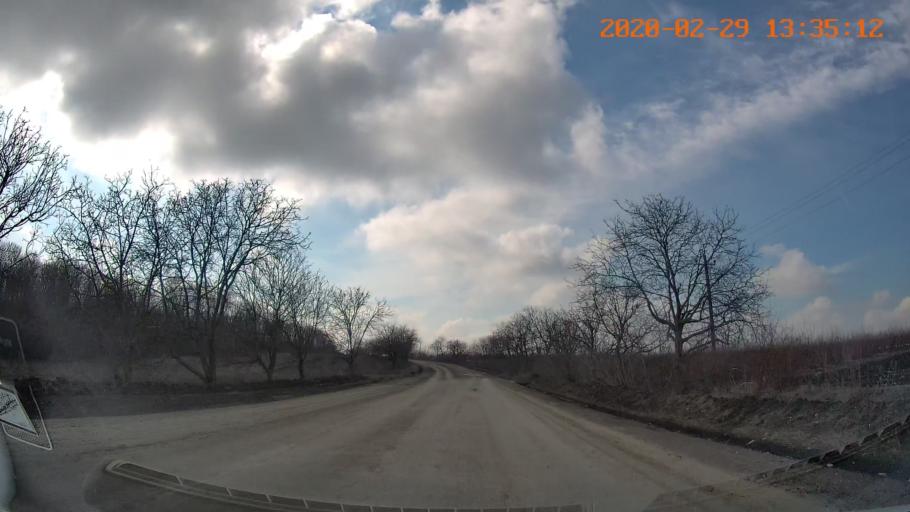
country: MD
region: Telenesti
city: Camenca
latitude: 47.8668
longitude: 28.6156
